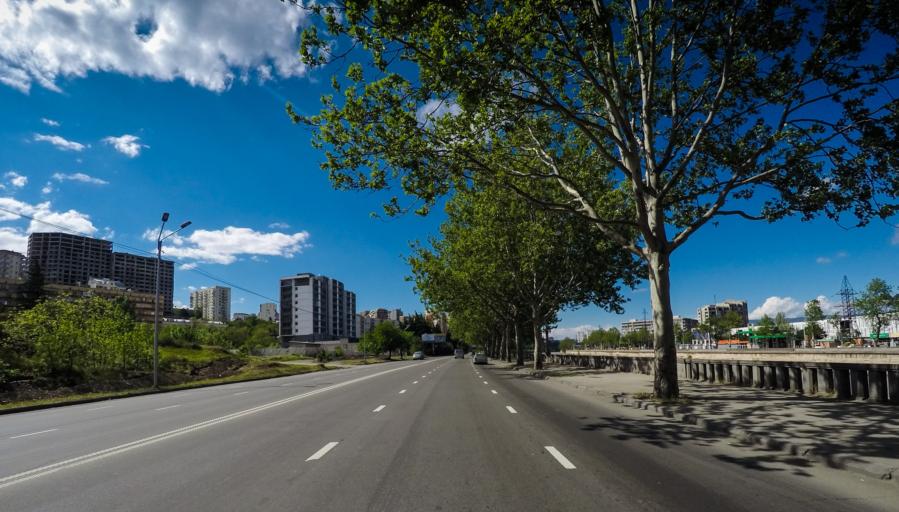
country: GE
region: T'bilisi
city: Tbilisi
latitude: 41.7304
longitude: 44.7753
